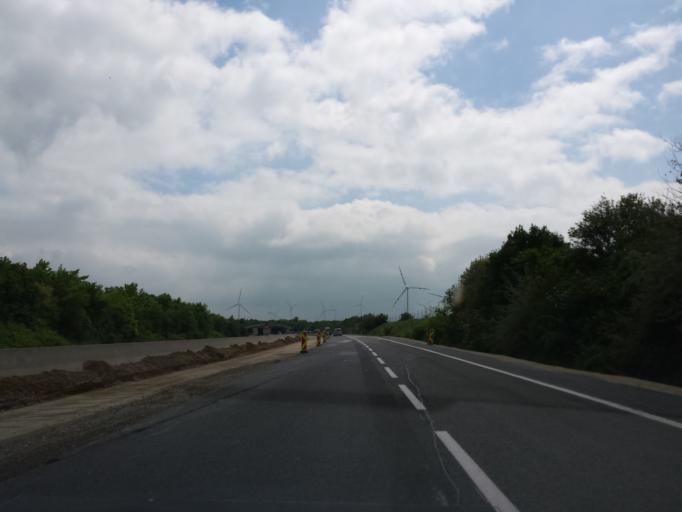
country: AT
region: Burgenland
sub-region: Politischer Bezirk Neusiedl am See
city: Gols
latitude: 47.9462
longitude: 16.9381
